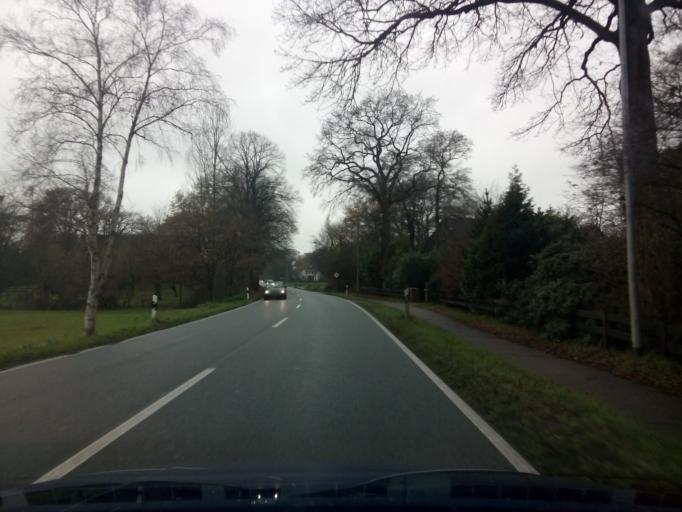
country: DE
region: Lower Saxony
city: Lilienthal
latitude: 53.1726
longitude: 8.9159
